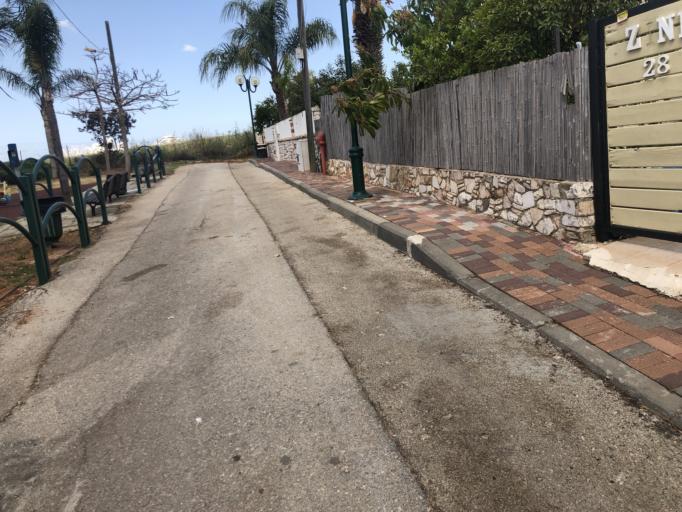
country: IL
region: Central District
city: Hod HaSharon
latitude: 32.1533
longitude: 34.9130
